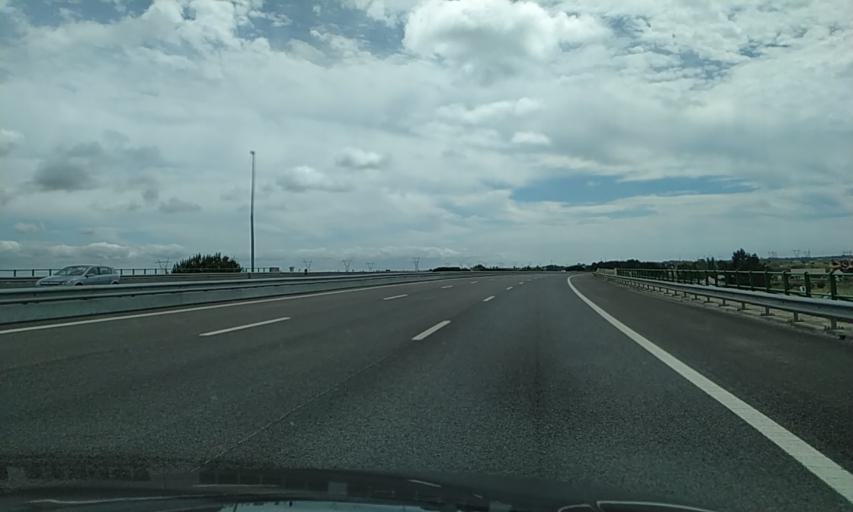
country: PT
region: Setubal
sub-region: Palmela
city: Pinhal Novo
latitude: 38.6316
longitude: -8.8670
